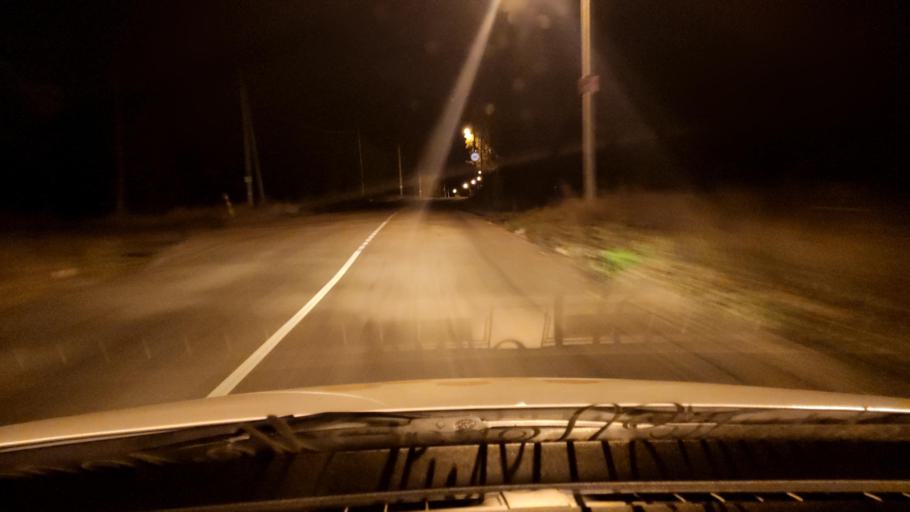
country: RU
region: Voronezj
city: Pridonskoy
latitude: 51.6967
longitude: 39.1049
